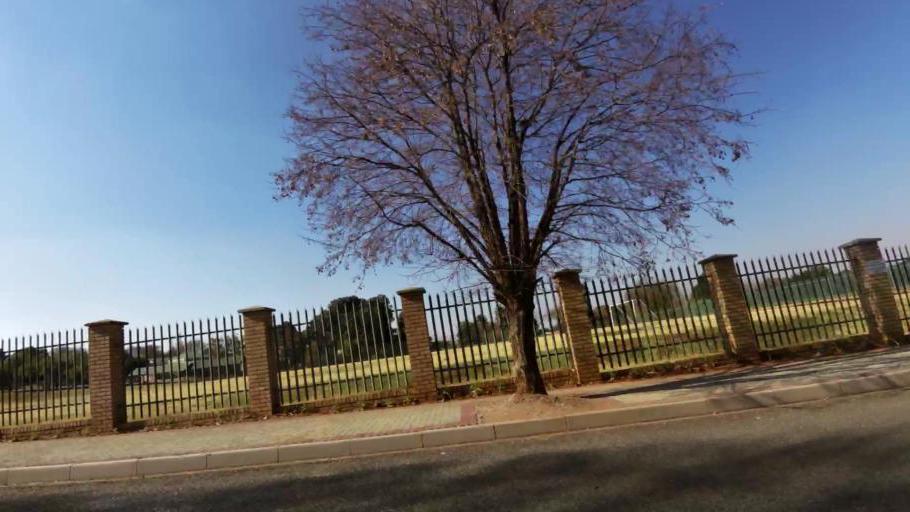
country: ZA
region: Gauteng
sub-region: City of Johannesburg Metropolitan Municipality
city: Johannesburg
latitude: -26.1729
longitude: 27.9847
